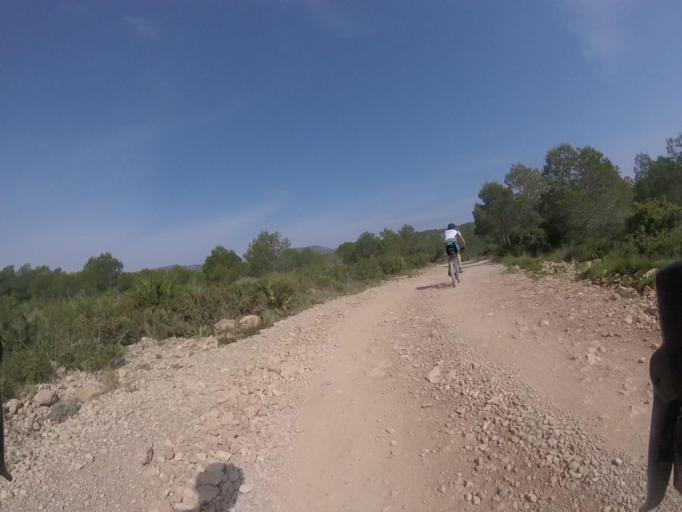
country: ES
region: Valencia
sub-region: Provincia de Castello
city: Alcoceber
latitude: 40.2838
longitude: 0.3253
